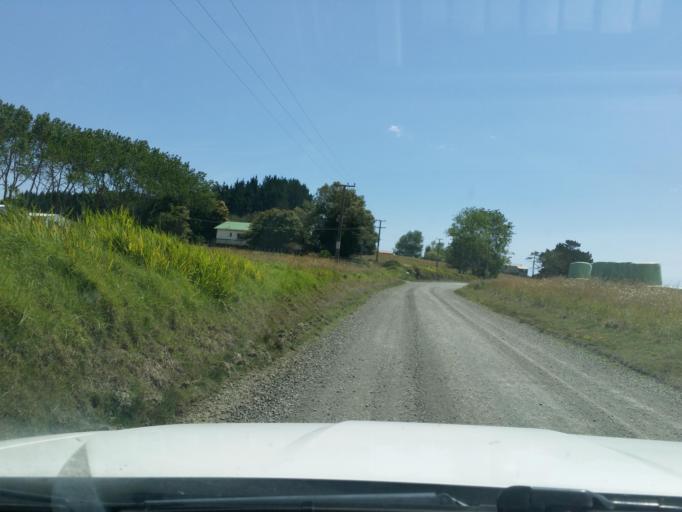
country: NZ
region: Northland
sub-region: Kaipara District
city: Dargaville
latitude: -35.9077
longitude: 173.7977
